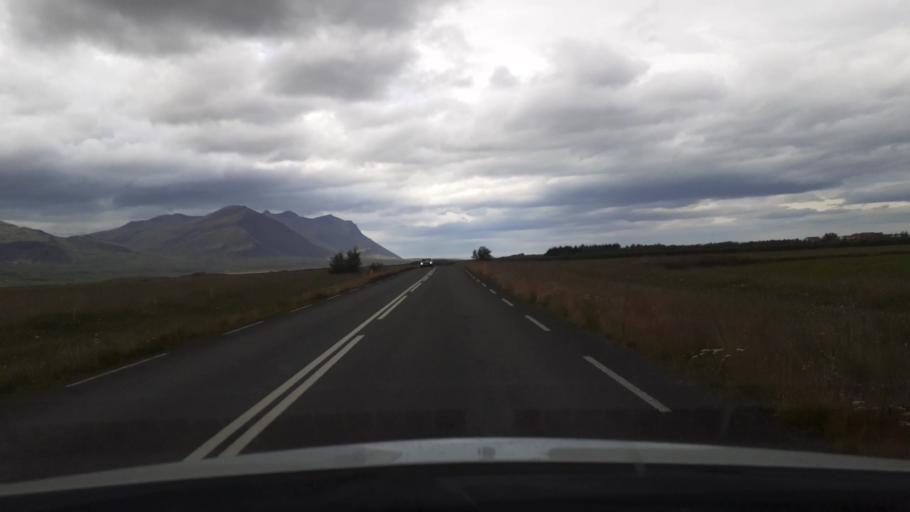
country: IS
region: West
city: Borgarnes
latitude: 64.5614
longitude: -21.7404
